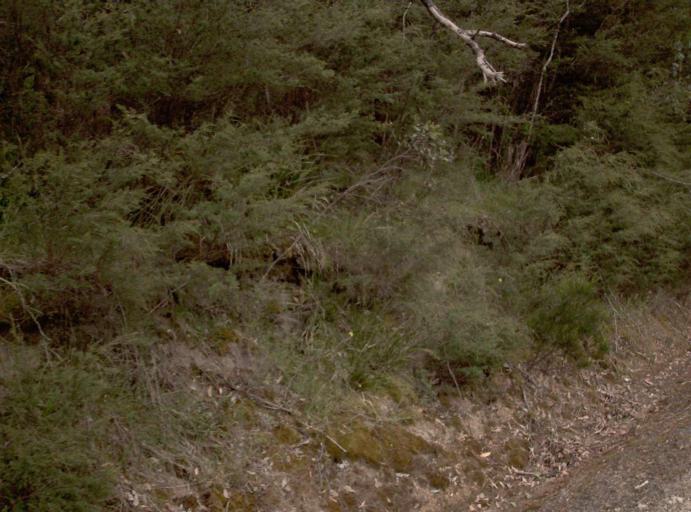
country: AU
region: New South Wales
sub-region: Bombala
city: Bombala
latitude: -37.3798
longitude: 149.2043
